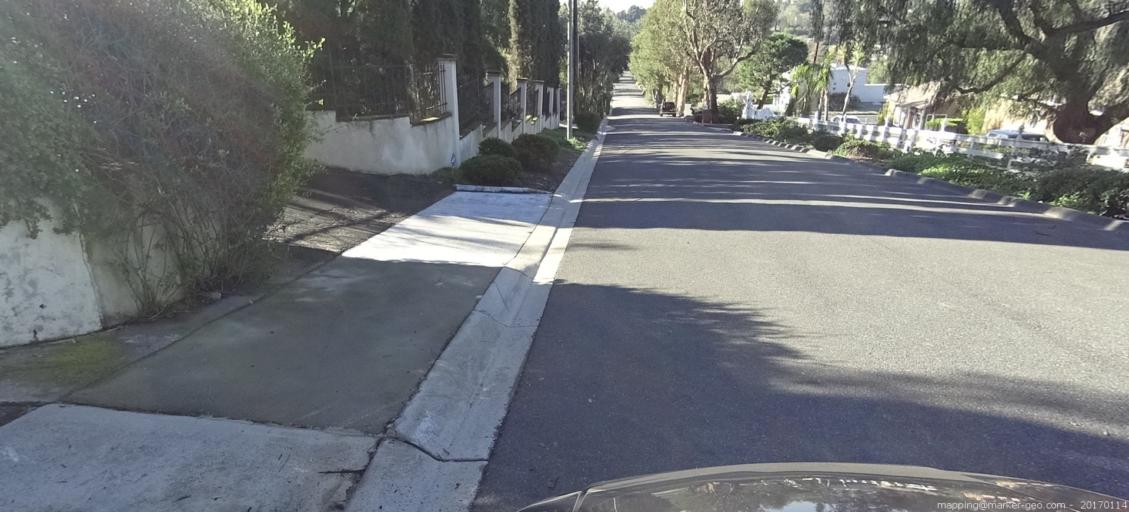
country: US
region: California
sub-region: Orange County
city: North Tustin
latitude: 33.7805
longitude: -117.7861
